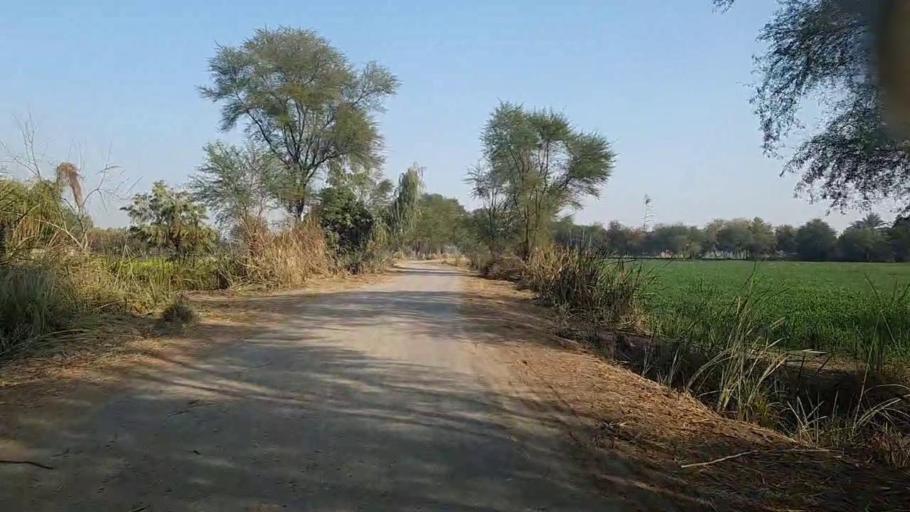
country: PK
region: Sindh
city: Mirpur Mathelo
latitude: 27.8765
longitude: 69.6193
